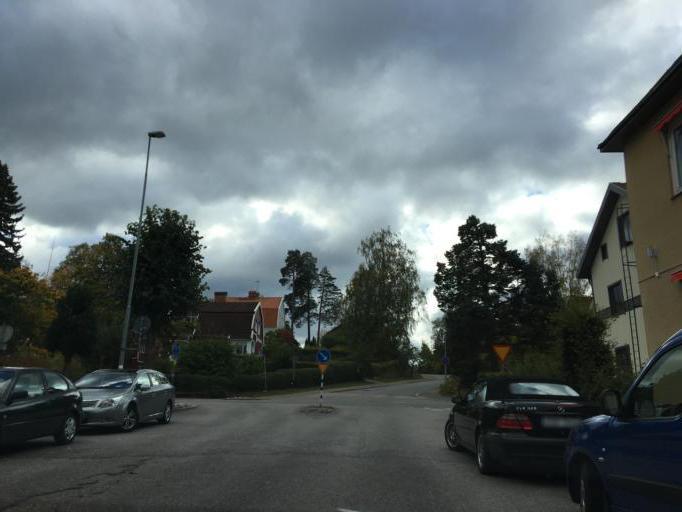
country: SE
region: Soedermanland
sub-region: Katrineholms Kommun
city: Katrineholm
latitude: 58.9923
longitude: 16.2008
